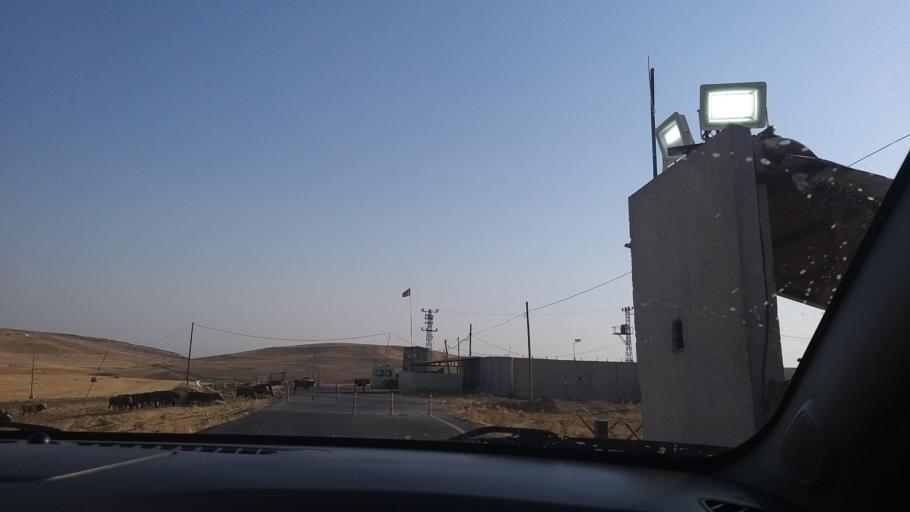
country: TR
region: Diyarbakir
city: Silvan
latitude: 38.1857
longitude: 41.0065
